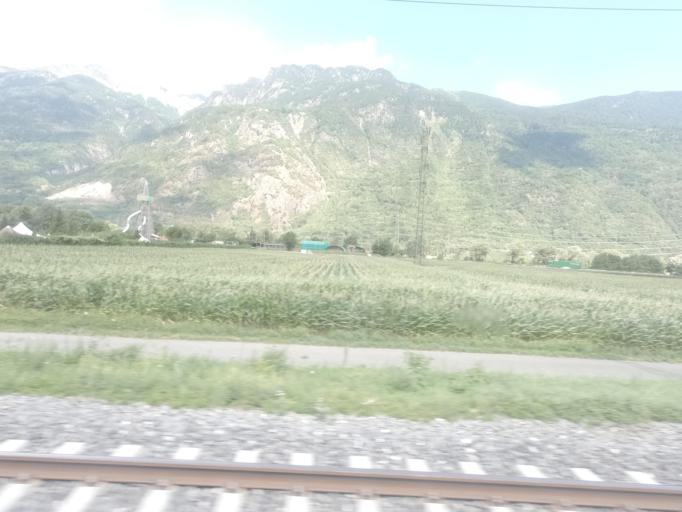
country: CH
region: Valais
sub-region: Martigny District
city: Evionnaz
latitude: 46.1633
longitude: 7.0284
